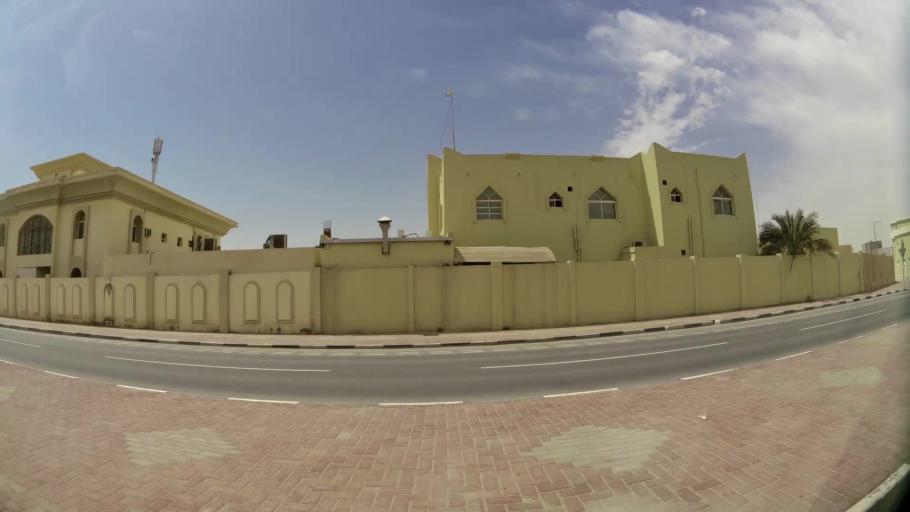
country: QA
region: Baladiyat ar Rayyan
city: Ar Rayyan
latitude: 25.2910
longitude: 51.4148
